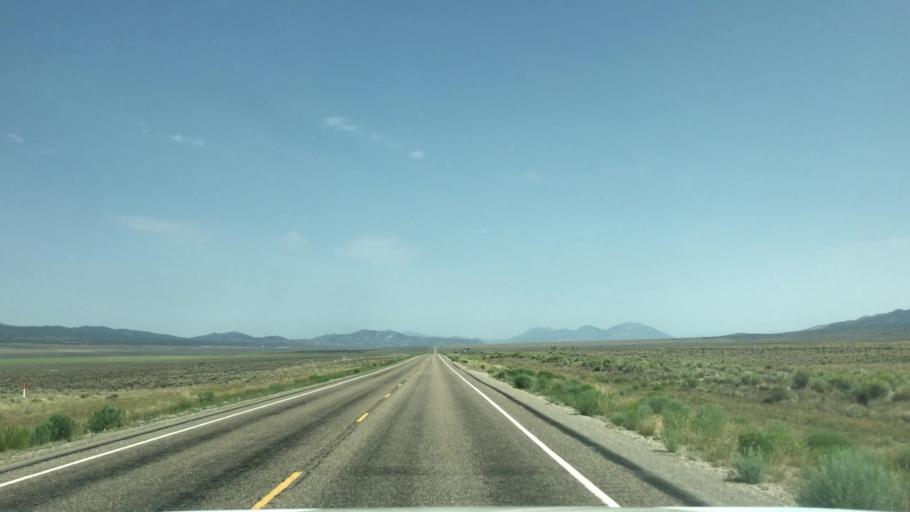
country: US
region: Nevada
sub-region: White Pine County
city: Ely
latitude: 39.0950
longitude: -114.7565
